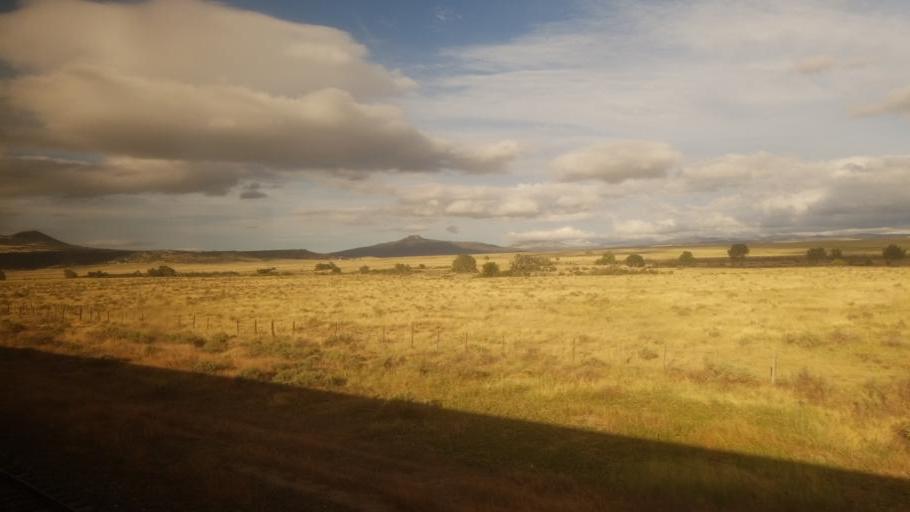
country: US
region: New Mexico
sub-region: Colfax County
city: Raton
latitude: 36.6325
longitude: -104.5024
